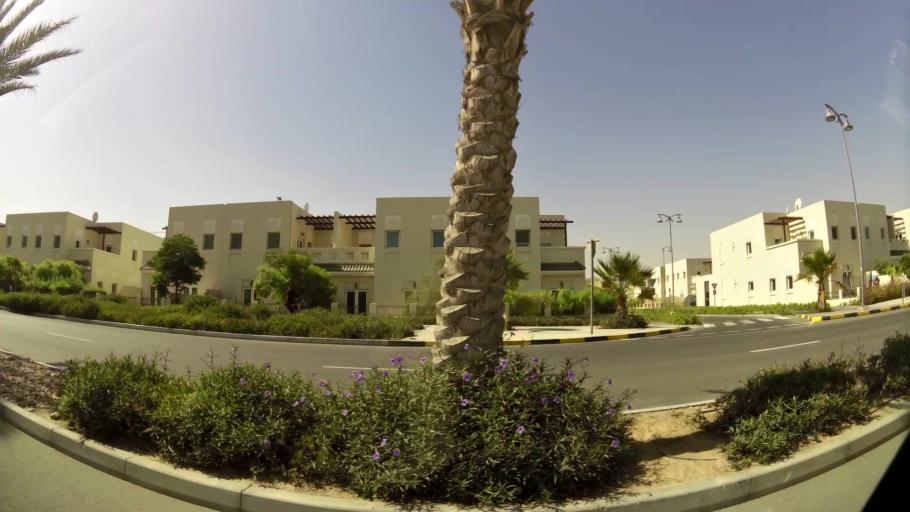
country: AE
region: Dubai
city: Dubai
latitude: 25.0233
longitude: 55.1523
